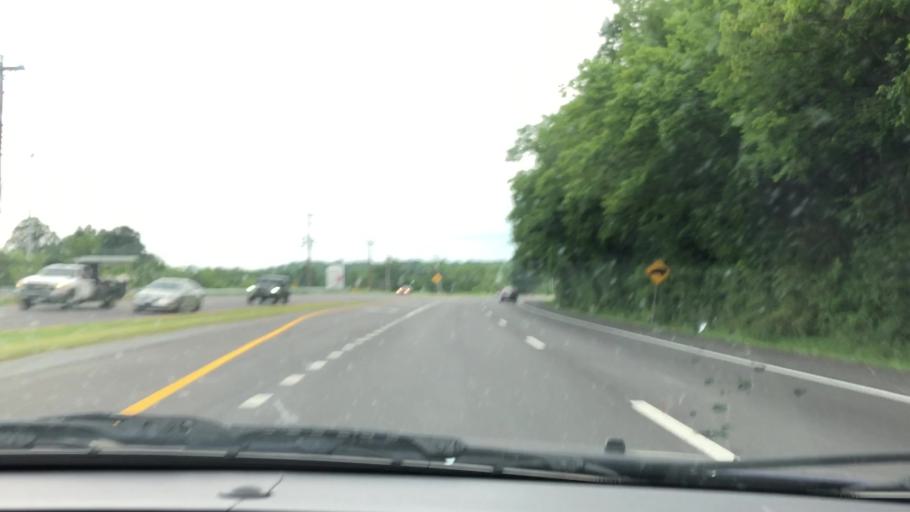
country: US
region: Tennessee
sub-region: Maury County
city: Columbia
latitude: 35.6662
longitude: -87.0057
